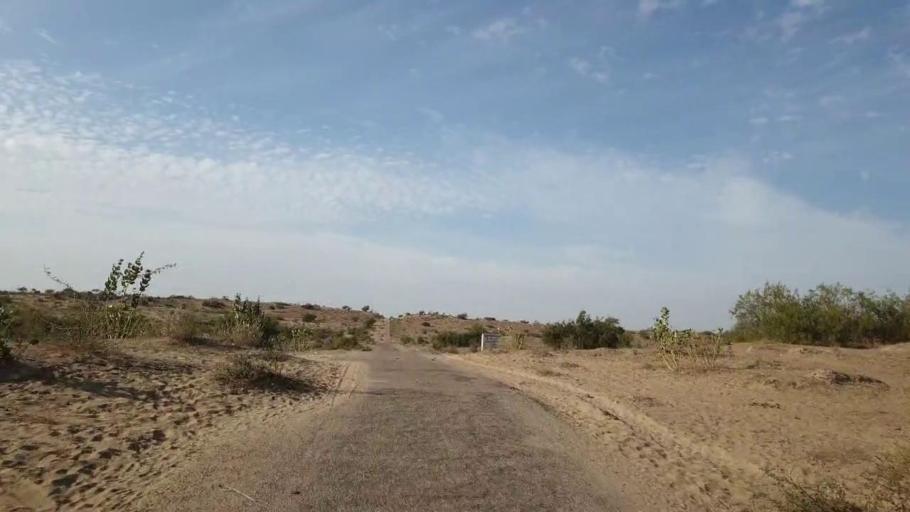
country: PK
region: Sindh
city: Nabisar
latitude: 25.0027
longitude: 69.9238
